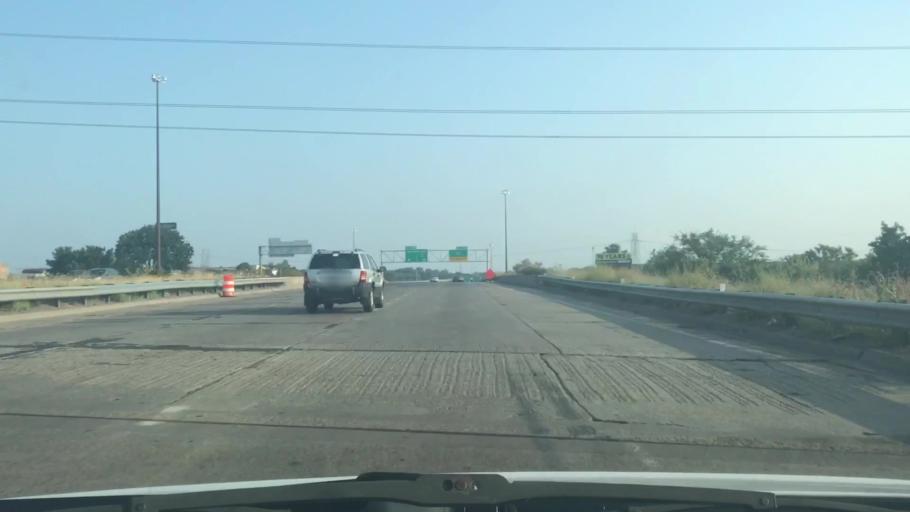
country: US
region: Minnesota
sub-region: Hennepin County
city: Saint Anthony
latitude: 45.0220
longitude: -93.1916
